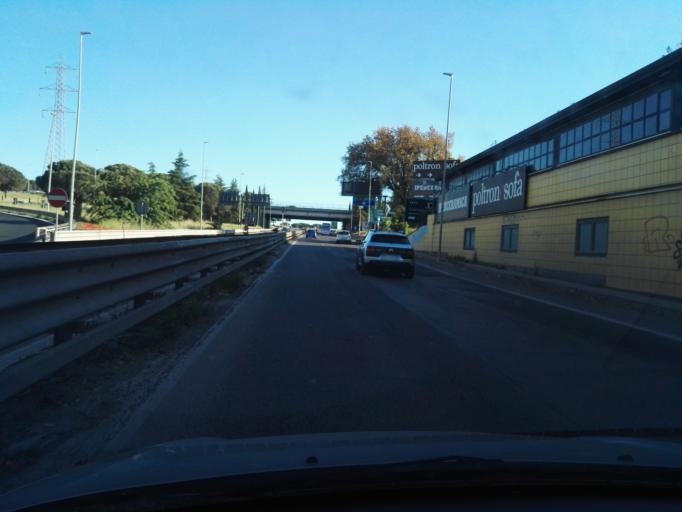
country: IT
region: Latium
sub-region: Citta metropolitana di Roma Capitale
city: Selcetta
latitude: 41.7996
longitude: 12.4810
